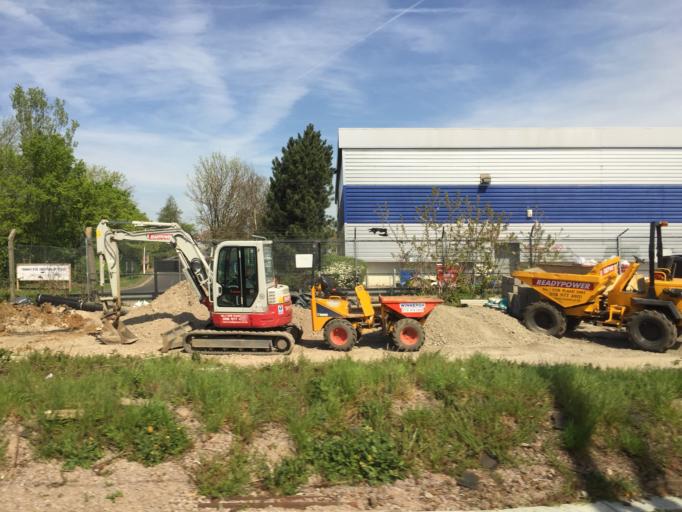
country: GB
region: England
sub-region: Greater London
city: Chadwell Heath
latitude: 51.5663
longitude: 0.1165
